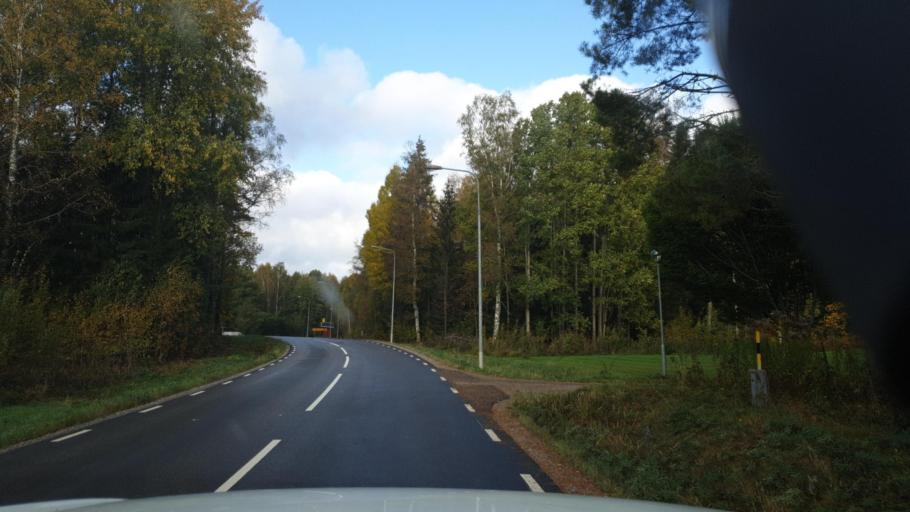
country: SE
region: Vaermland
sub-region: Arvika Kommun
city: Arvika
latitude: 59.5342
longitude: 12.5983
